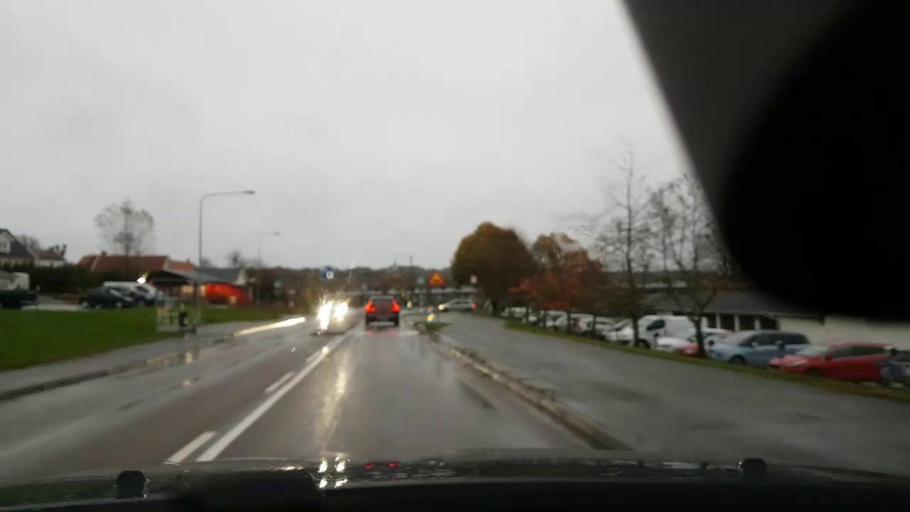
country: SE
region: Vaestra Goetaland
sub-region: Molndal
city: Lindome
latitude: 57.5854
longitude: 12.0946
